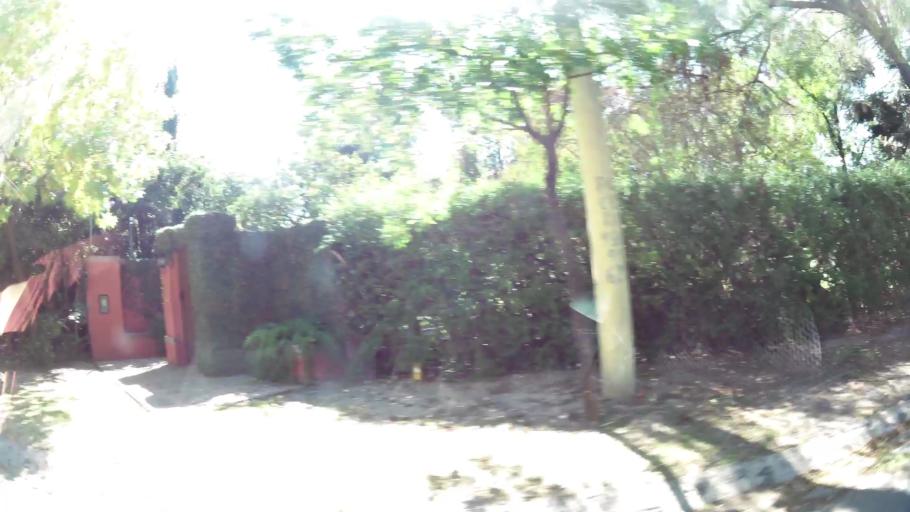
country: AR
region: Cordoba
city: Villa Allende
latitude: -31.2911
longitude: -64.2828
